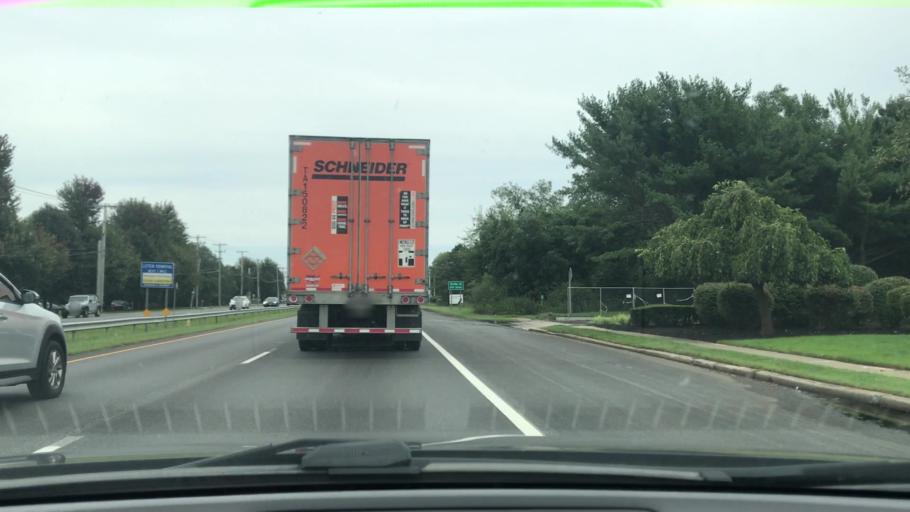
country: US
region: New York
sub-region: Suffolk County
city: Bohemia
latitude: 40.7835
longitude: -73.1052
